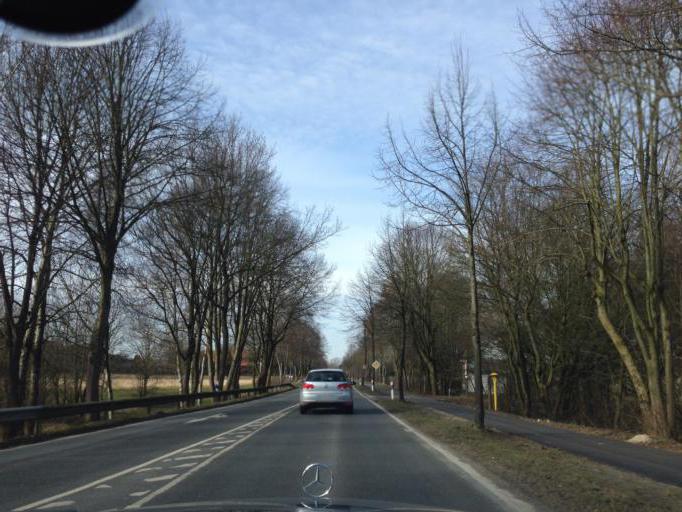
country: DE
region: Lower Saxony
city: Seevetal
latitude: 53.4380
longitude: 9.9131
